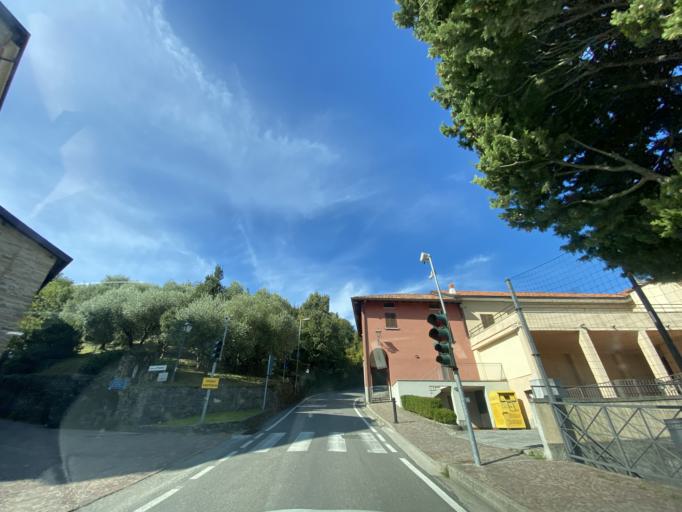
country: IT
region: Lombardy
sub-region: Provincia di Lecco
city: Montevecchia
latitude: 45.7055
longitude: 9.3808
